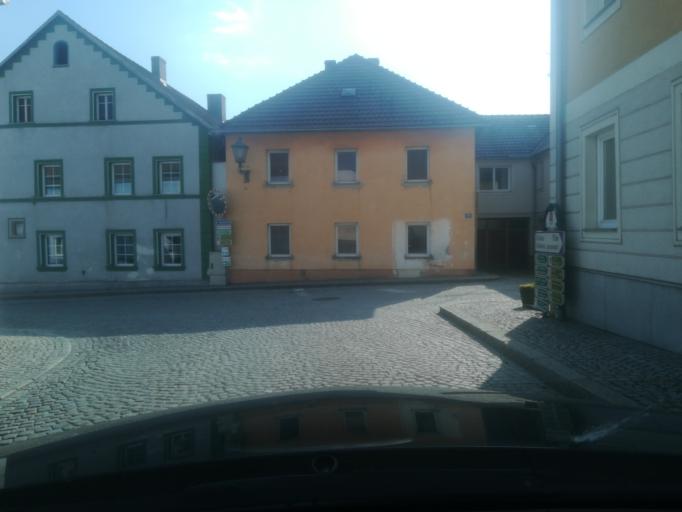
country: AT
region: Upper Austria
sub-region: Politischer Bezirk Perg
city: Perg
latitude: 48.3505
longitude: 14.6685
